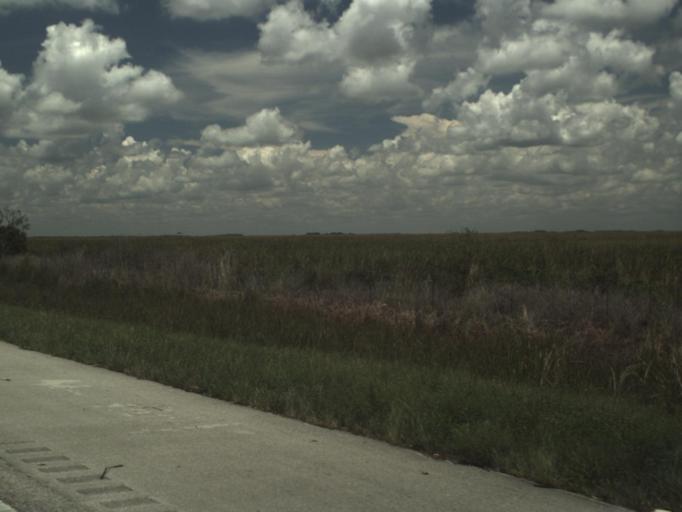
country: US
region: Florida
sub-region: Broward County
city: Weston
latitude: 26.1555
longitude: -80.7569
